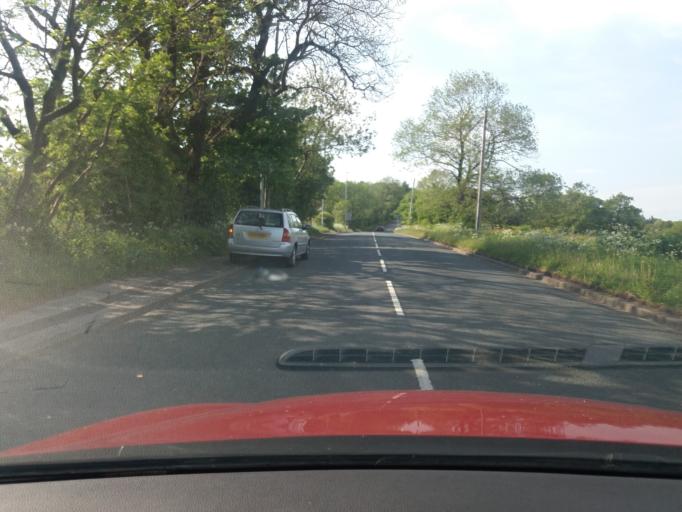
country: GB
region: England
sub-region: Blackburn with Darwen
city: Blackburn
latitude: 53.7026
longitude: -2.5494
